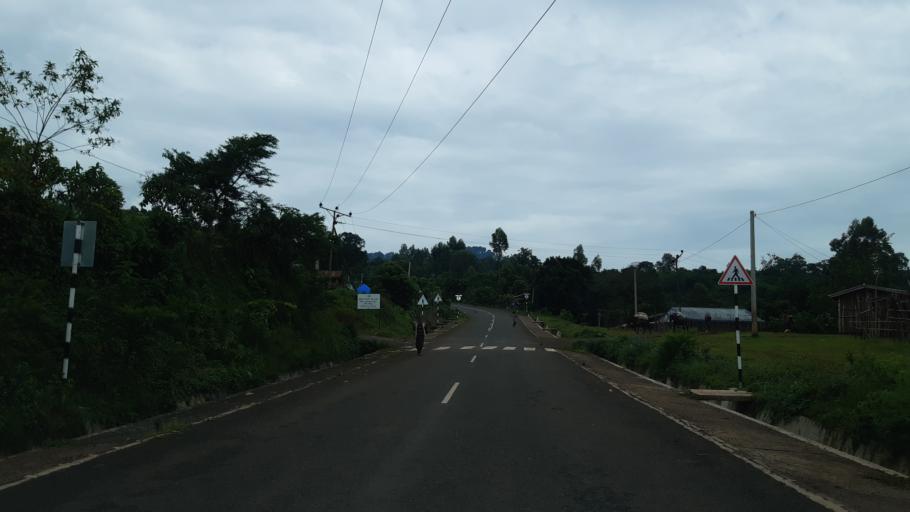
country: ET
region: Southern Nations, Nationalities, and People's Region
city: Bonga
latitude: 7.1936
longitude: 36.3028
